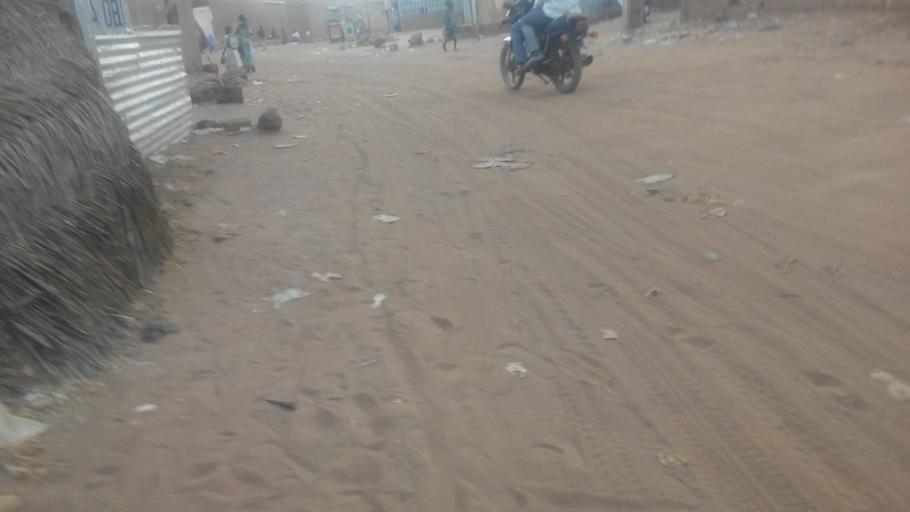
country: NE
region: Niamey
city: Niamey
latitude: 13.5512
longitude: 2.0539
